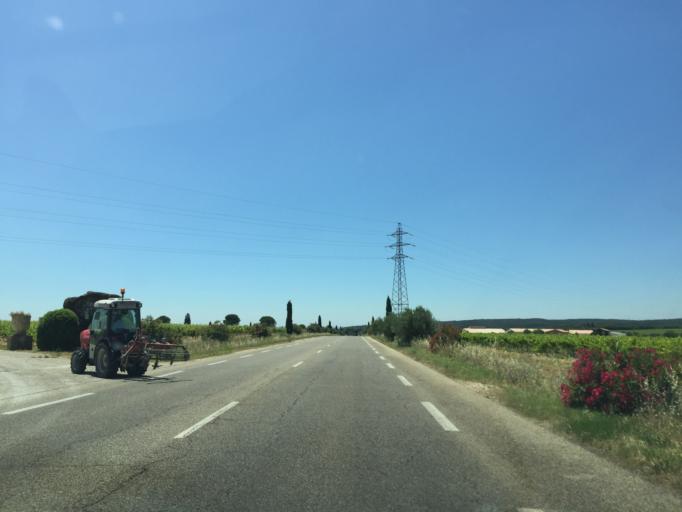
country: FR
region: Provence-Alpes-Cote d'Azur
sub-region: Departement du Vaucluse
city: Sainte-Cecile-les-Vignes
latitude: 44.2177
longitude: 4.8749
